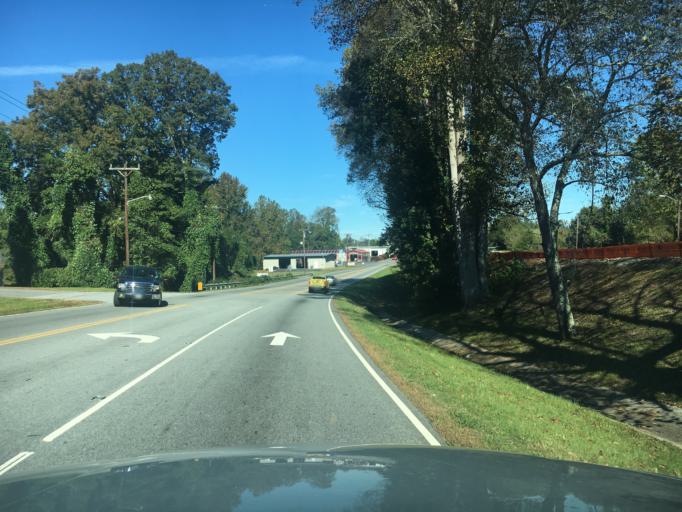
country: US
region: North Carolina
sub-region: Rutherford County
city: Rutherfordton
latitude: 35.3782
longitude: -81.9465
